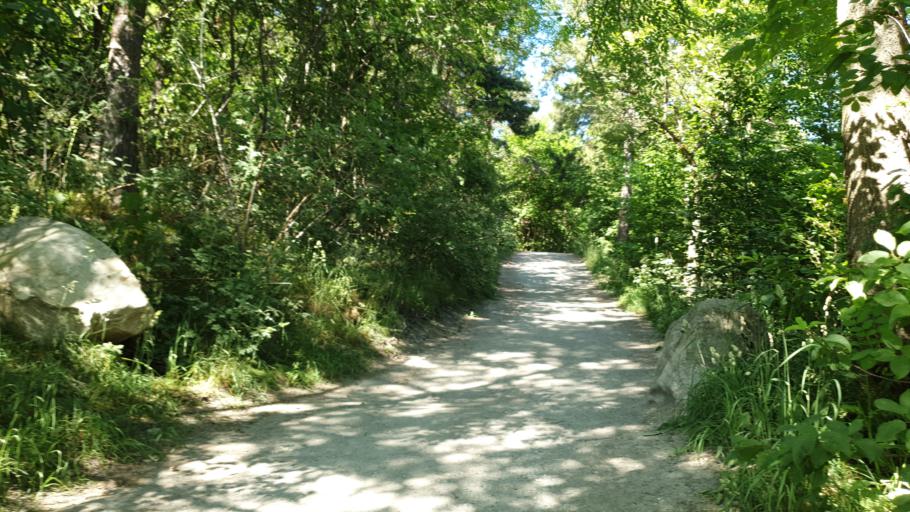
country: NO
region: Sor-Trondelag
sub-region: Trondheim
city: Trondheim
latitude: 63.4426
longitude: 10.4705
